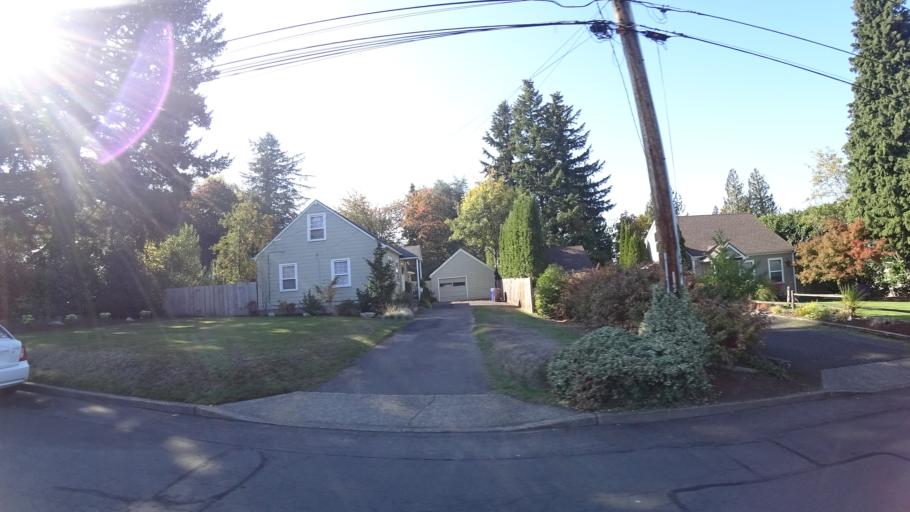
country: US
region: Oregon
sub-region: Multnomah County
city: Gresham
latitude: 45.5037
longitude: -122.4492
